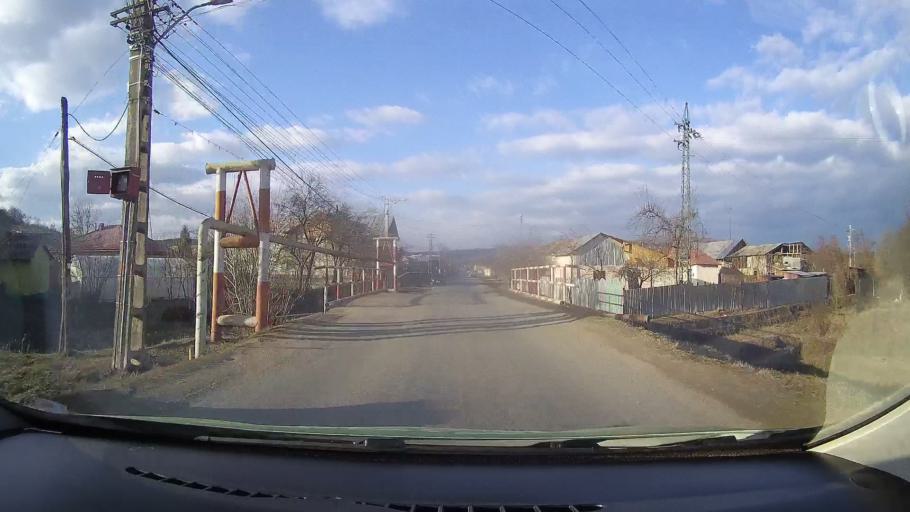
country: RO
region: Dambovita
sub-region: Comuna Ocnita
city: Ocnita
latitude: 44.9759
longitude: 25.5561
